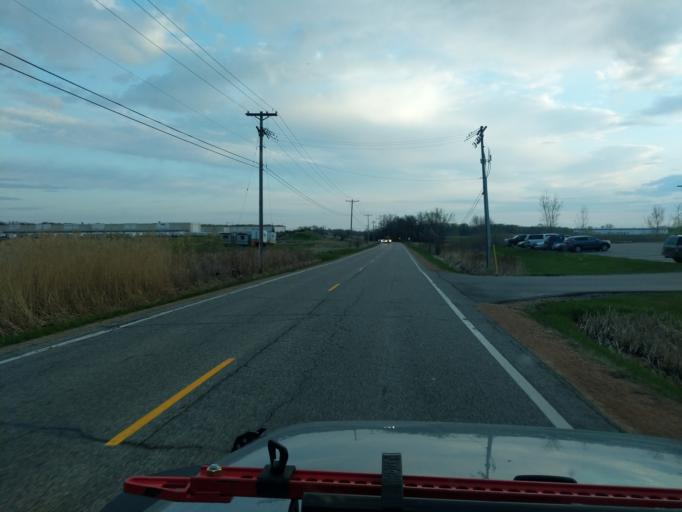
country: US
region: Minnesota
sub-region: Hennepin County
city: Rogers
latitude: 45.1747
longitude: -93.5216
